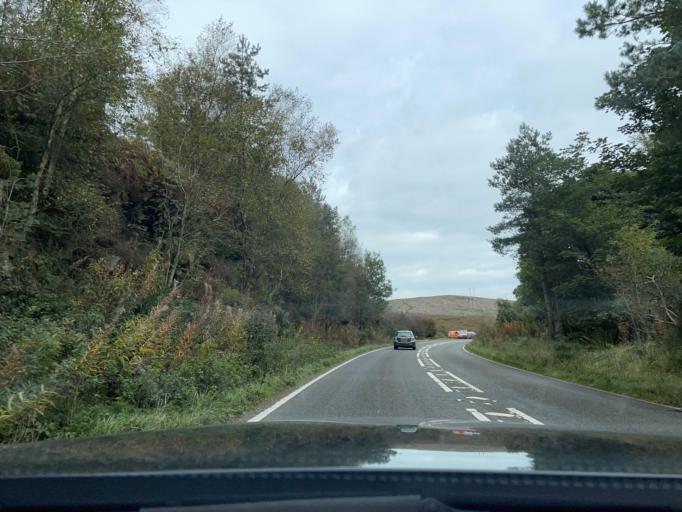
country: GB
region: England
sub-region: Derbyshire
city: Hathersage
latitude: 53.3818
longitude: -1.6819
